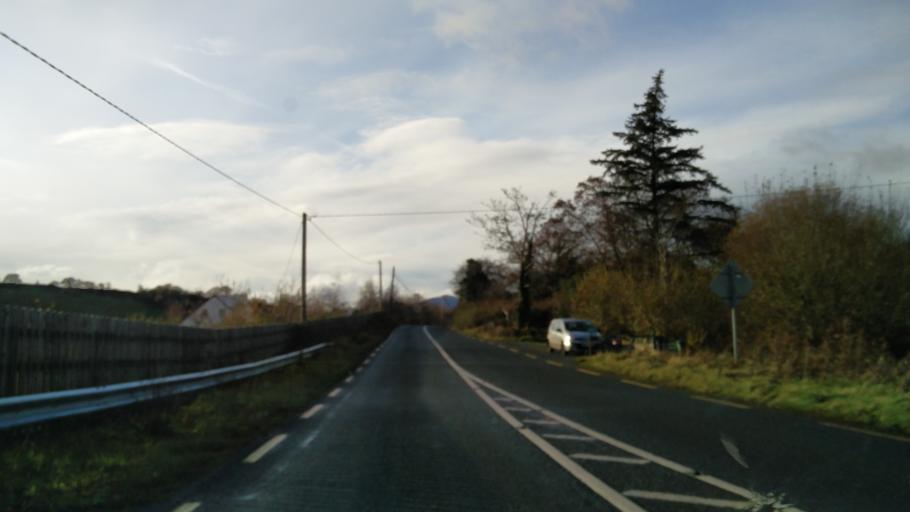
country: IE
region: Connaught
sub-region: Maigh Eo
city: Westport
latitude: 53.7839
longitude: -9.4737
